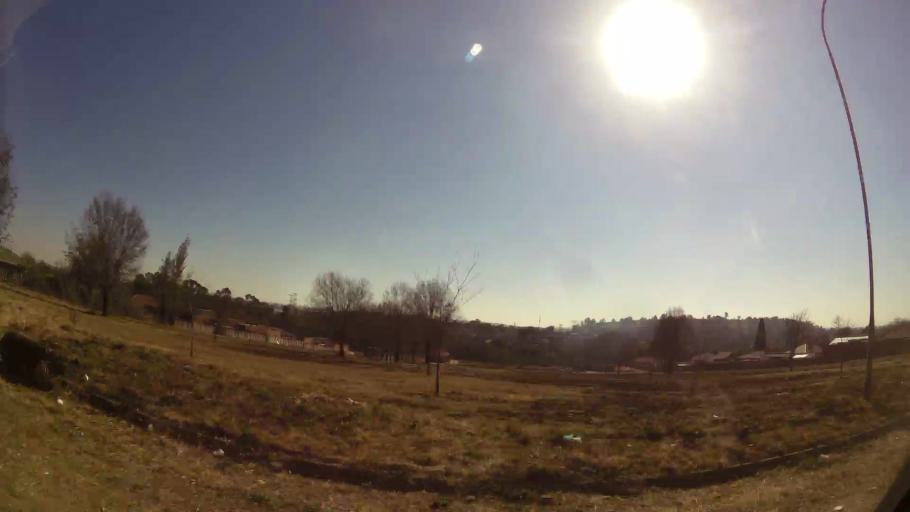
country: ZA
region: Gauteng
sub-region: City of Johannesburg Metropolitan Municipality
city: Johannesburg
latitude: -26.2401
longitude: 28.0924
